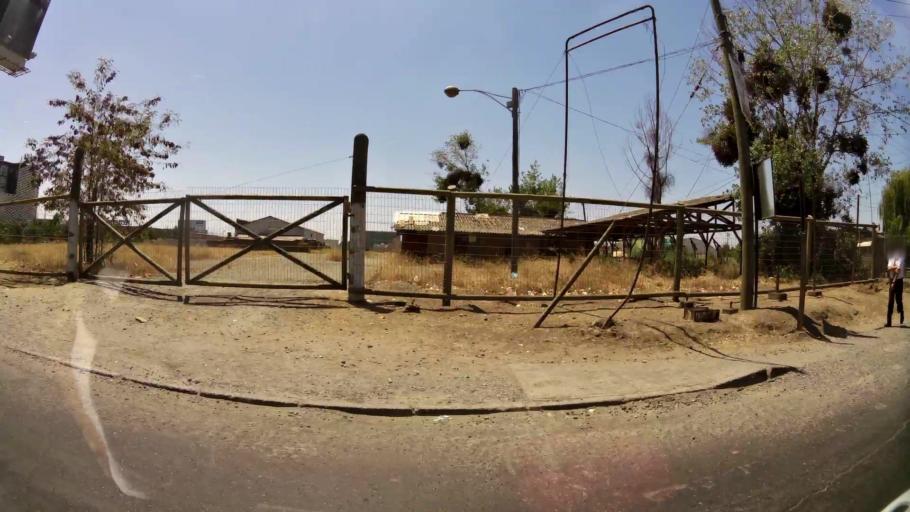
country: CL
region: Maule
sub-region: Provincia de Talca
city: Talca
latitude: -35.4342
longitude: -71.6282
